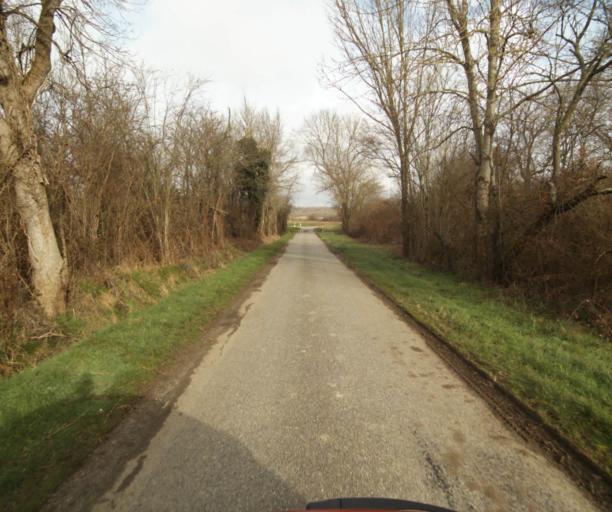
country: FR
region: Midi-Pyrenees
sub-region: Departement de l'Ariege
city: Saverdun
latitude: 43.1785
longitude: 1.5165
